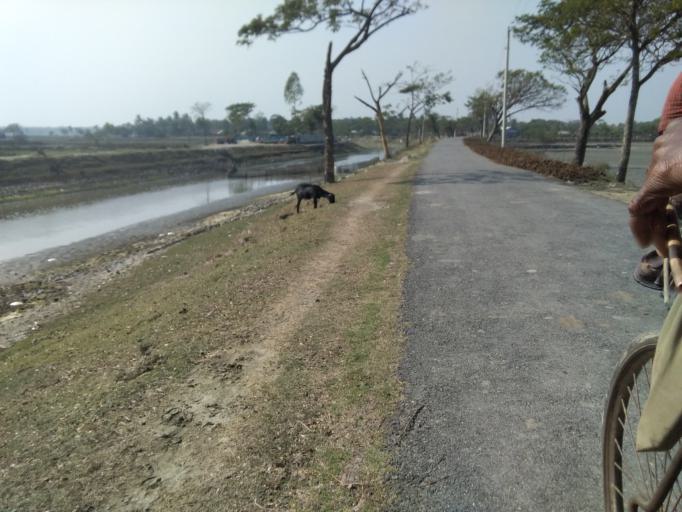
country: IN
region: West Bengal
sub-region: North 24 Parganas
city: Taki
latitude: 22.6361
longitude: 89.0048
